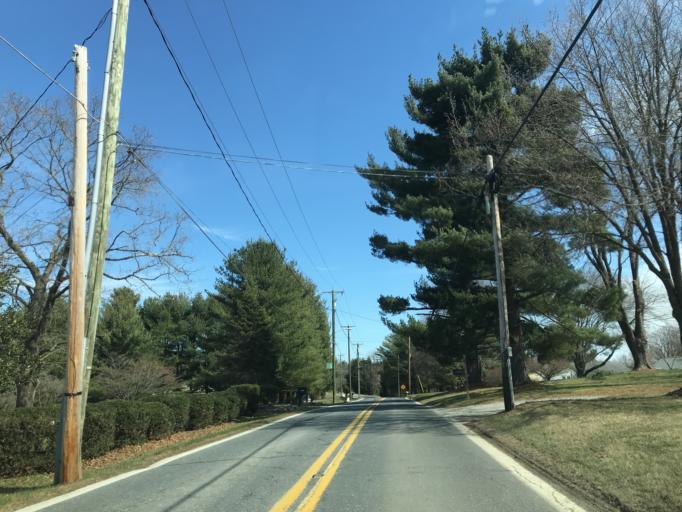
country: US
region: Maryland
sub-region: Montgomery County
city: Spencerville
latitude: 39.1400
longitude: -76.9746
